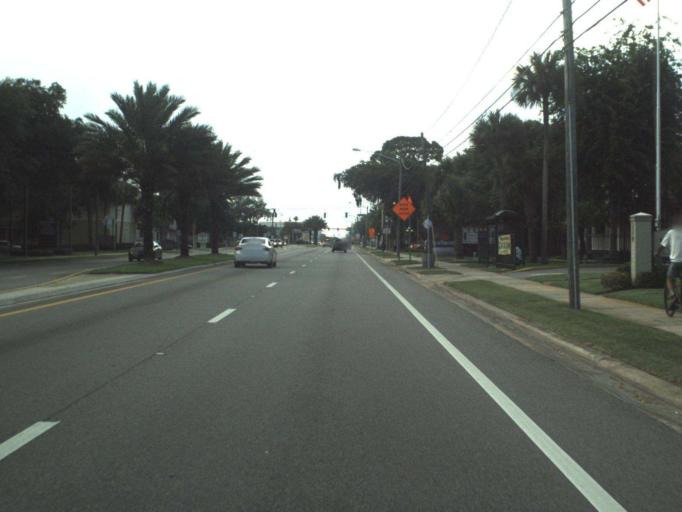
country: US
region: Florida
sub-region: Volusia County
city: Daytona Beach
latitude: 29.2076
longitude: -81.0210
